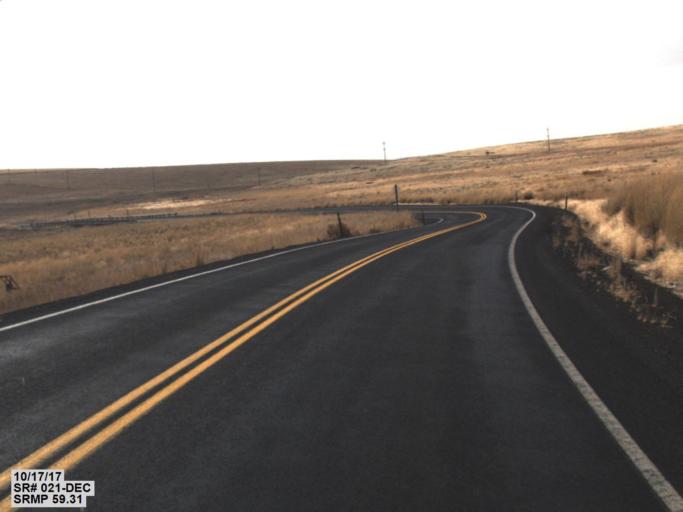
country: US
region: Washington
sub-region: Adams County
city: Ritzville
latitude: 47.3779
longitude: -118.6937
